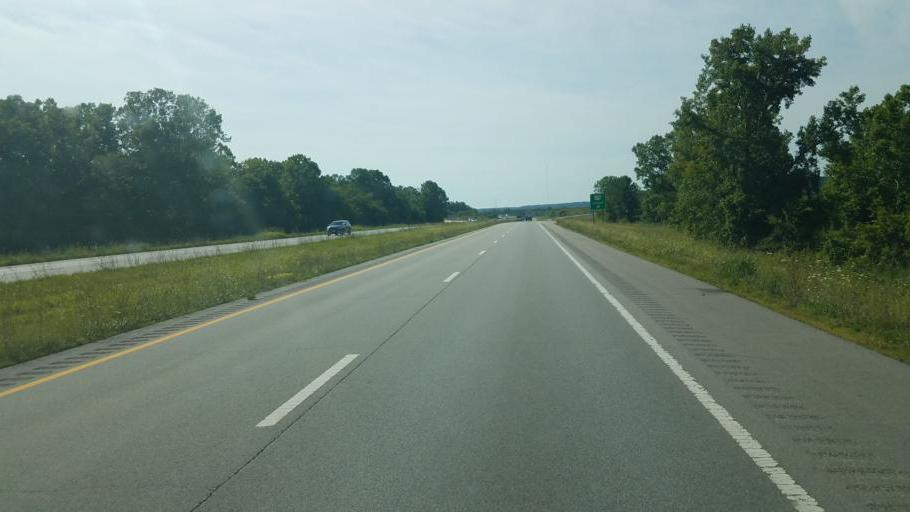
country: US
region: Ohio
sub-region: Hocking County
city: Logan
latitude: 39.5181
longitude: -82.3704
